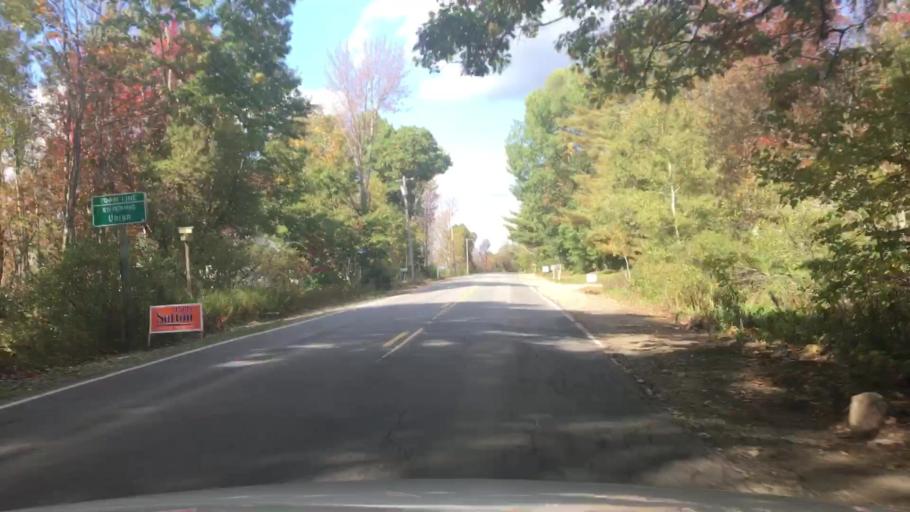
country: US
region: Maine
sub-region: Knox County
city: Union
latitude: 44.1811
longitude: -69.2594
